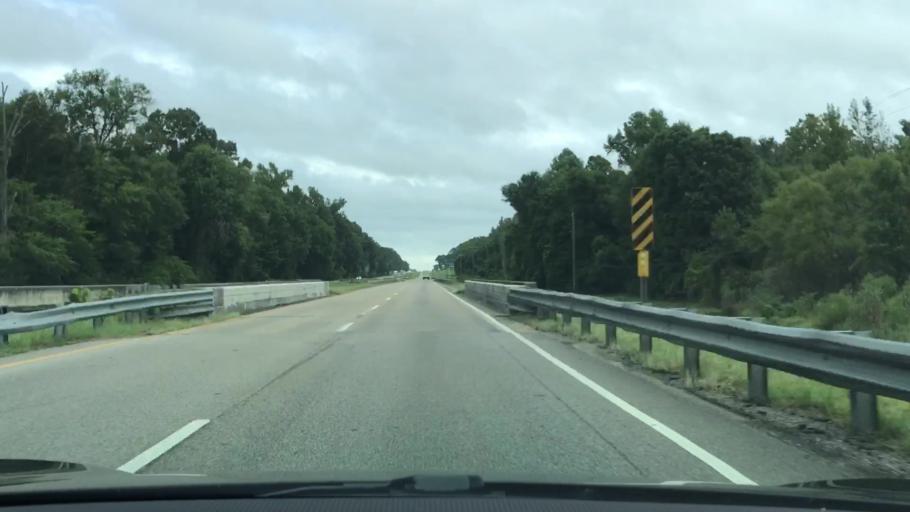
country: US
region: Alabama
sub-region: Montgomery County
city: Pike Road
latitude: 32.1824
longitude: -86.1172
